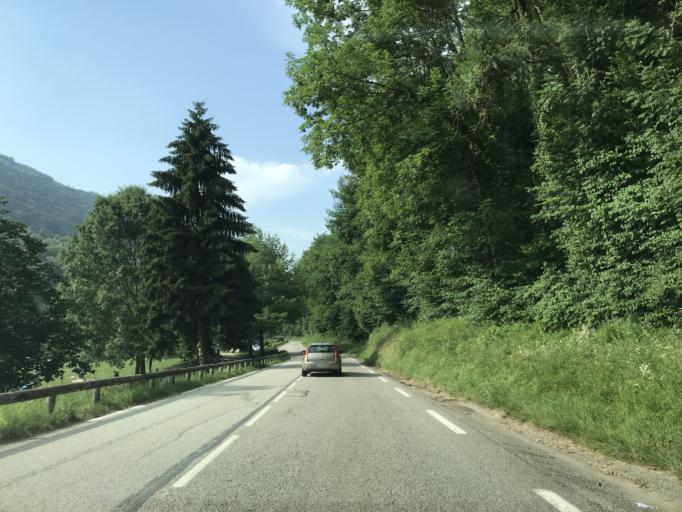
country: FR
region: Rhone-Alpes
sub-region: Departement de l'Isere
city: Allevard
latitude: 45.4078
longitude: 6.0865
